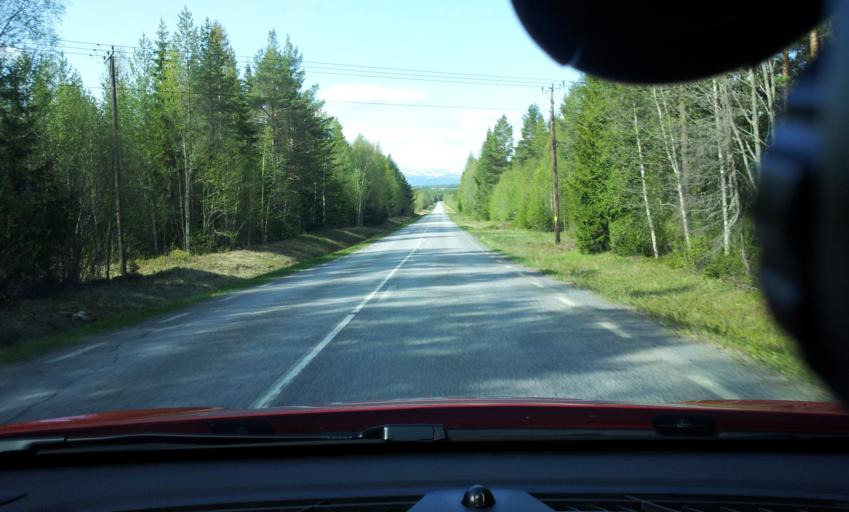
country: SE
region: Jaemtland
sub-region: Krokoms Kommun
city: Krokom
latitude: 63.1340
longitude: 14.2567
